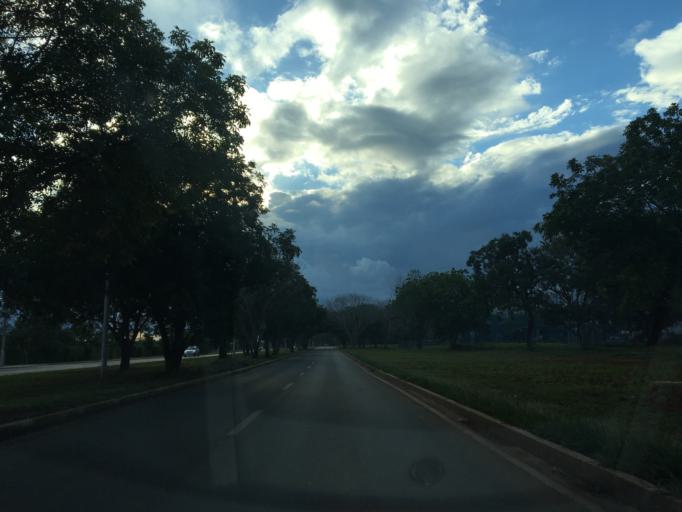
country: BR
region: Federal District
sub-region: Brasilia
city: Brasilia
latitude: -15.8157
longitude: -47.8590
